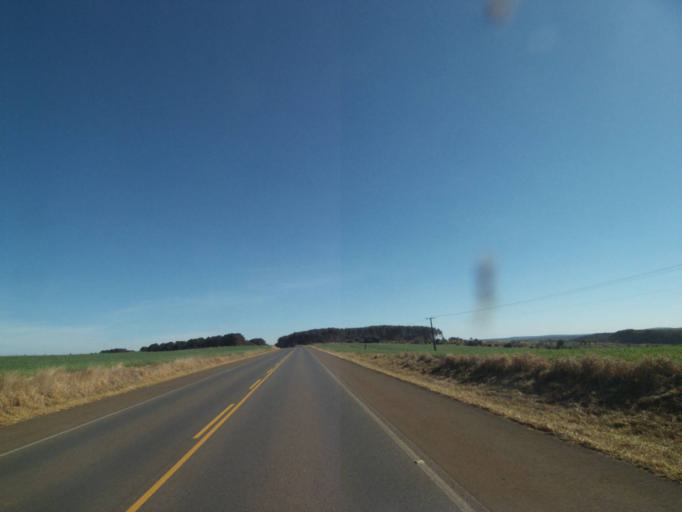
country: BR
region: Parana
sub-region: Tibagi
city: Tibagi
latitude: -24.4309
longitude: -50.4095
